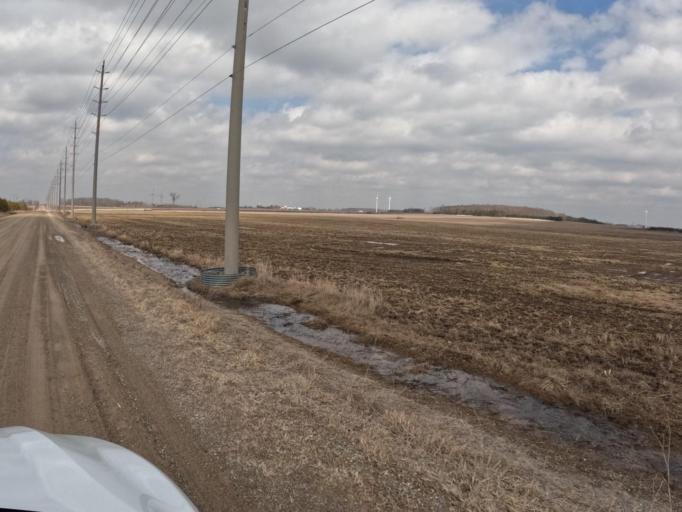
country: CA
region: Ontario
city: Shelburne
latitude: 44.0451
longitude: -80.3186
